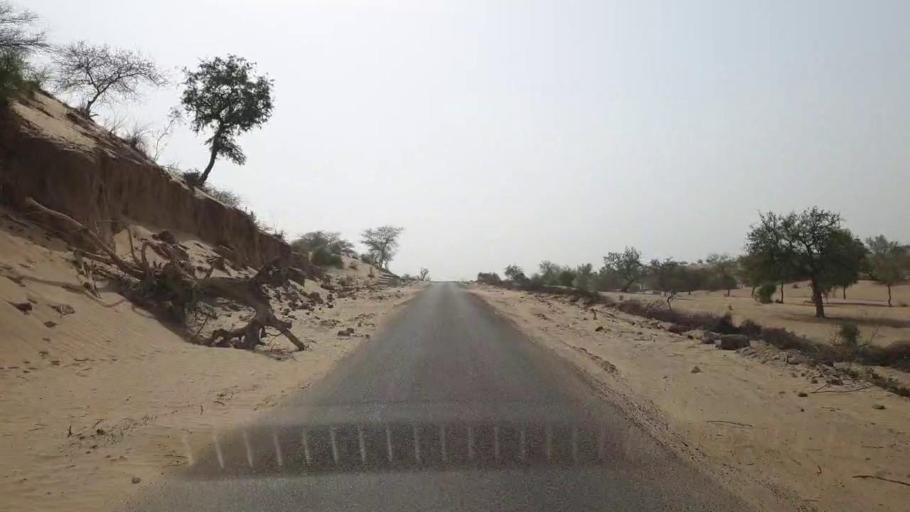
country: PK
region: Sindh
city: Mithi
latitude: 24.6201
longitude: 69.8798
